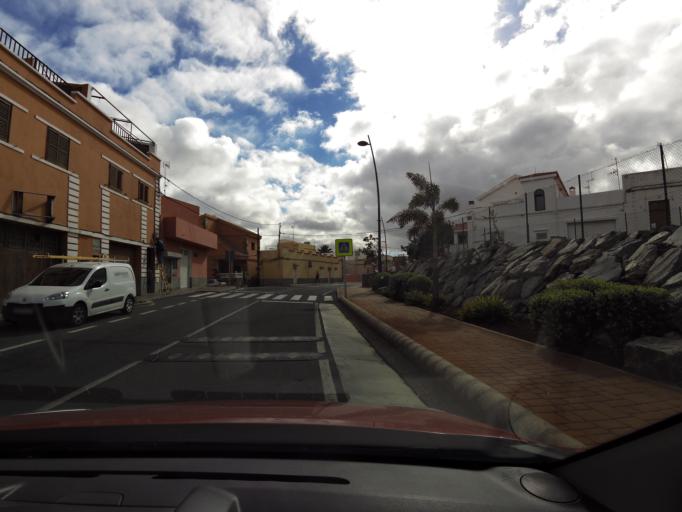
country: ES
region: Canary Islands
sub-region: Provincia de Las Palmas
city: Ingenio
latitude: 27.9217
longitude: -15.4360
